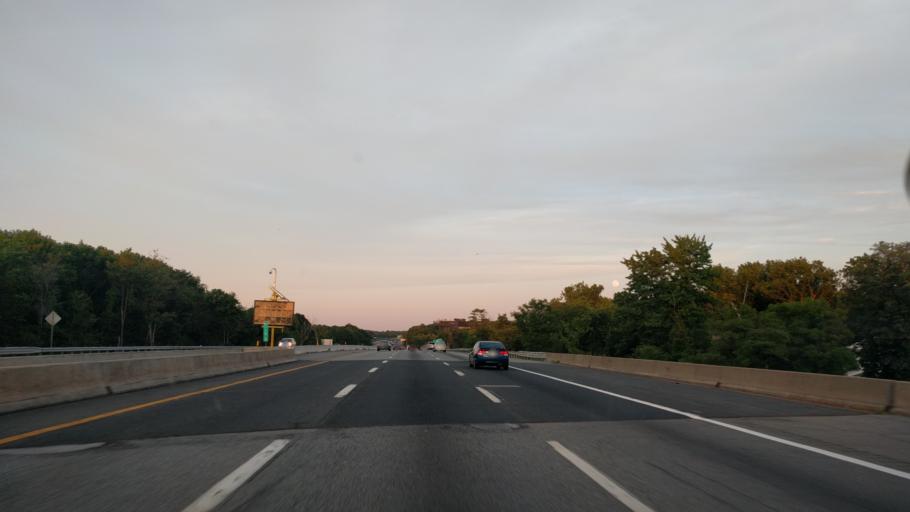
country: US
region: Massachusetts
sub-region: Middlesex County
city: Cochituate
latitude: 42.3154
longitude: -71.4012
